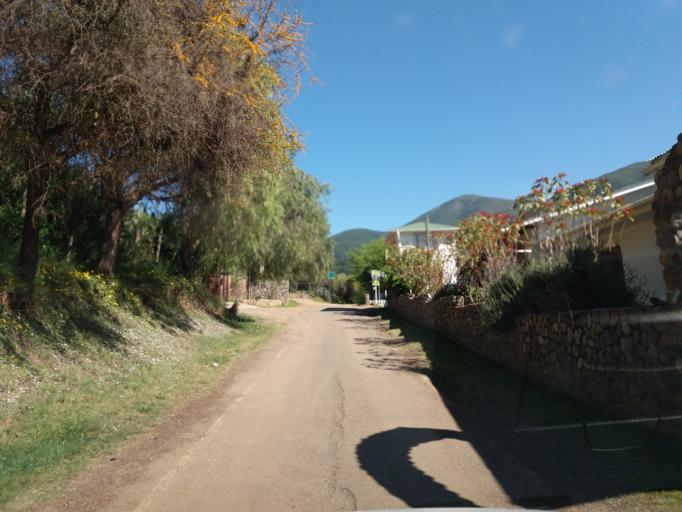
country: CL
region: Valparaiso
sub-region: Provincia de Quillota
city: Quillota
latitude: -32.8537
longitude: -71.2942
